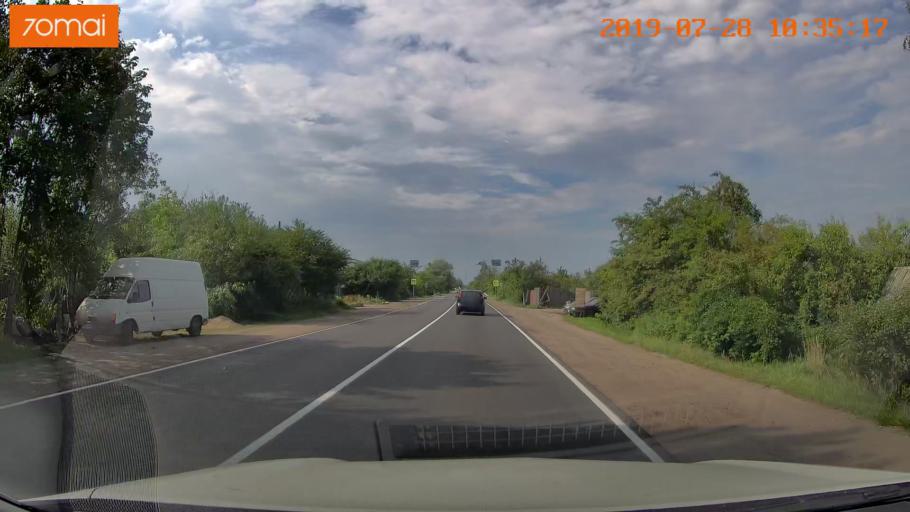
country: RU
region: Kaliningrad
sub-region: Gorod Kaliningrad
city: Kaliningrad
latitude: 54.7481
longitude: 20.4328
